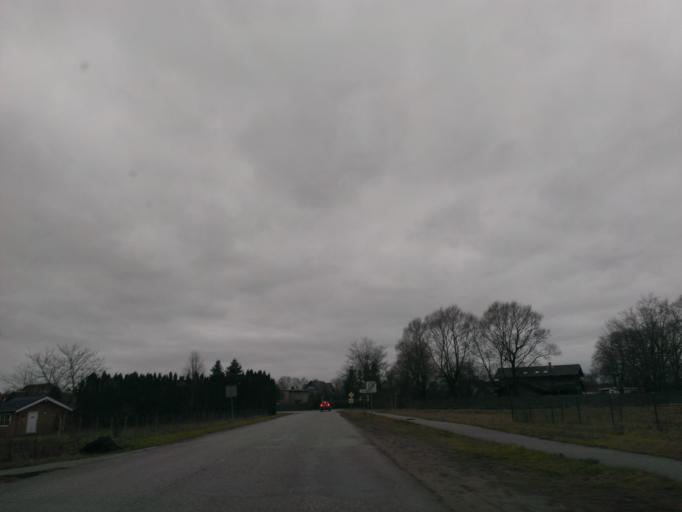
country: LV
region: Adazi
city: Adazi
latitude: 57.0705
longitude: 24.3388
